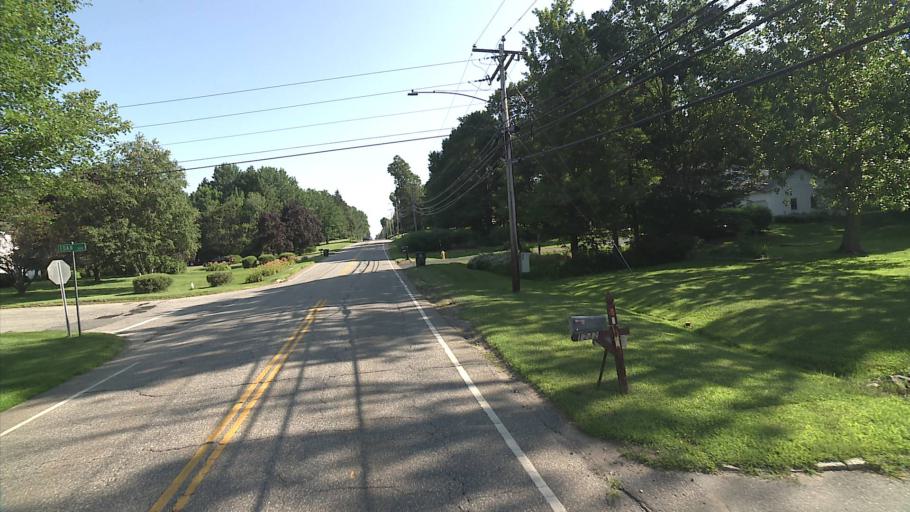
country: US
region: Connecticut
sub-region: Litchfield County
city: Torrington
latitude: 41.8248
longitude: -73.0799
